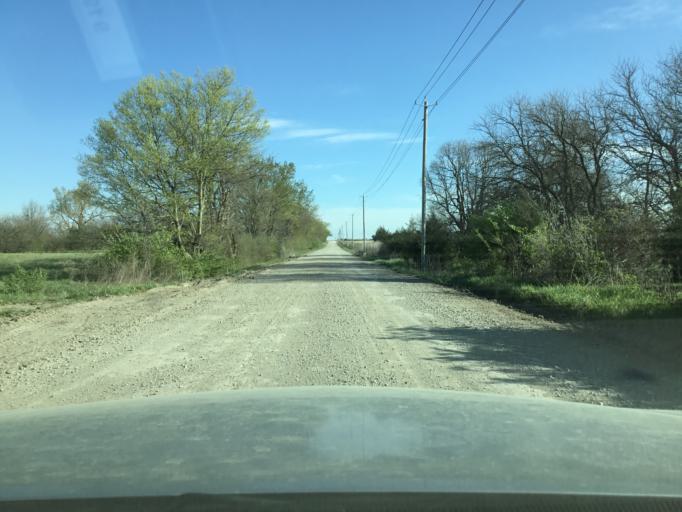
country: US
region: Kansas
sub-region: Neosho County
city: Chanute
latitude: 37.6546
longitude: -95.4893
